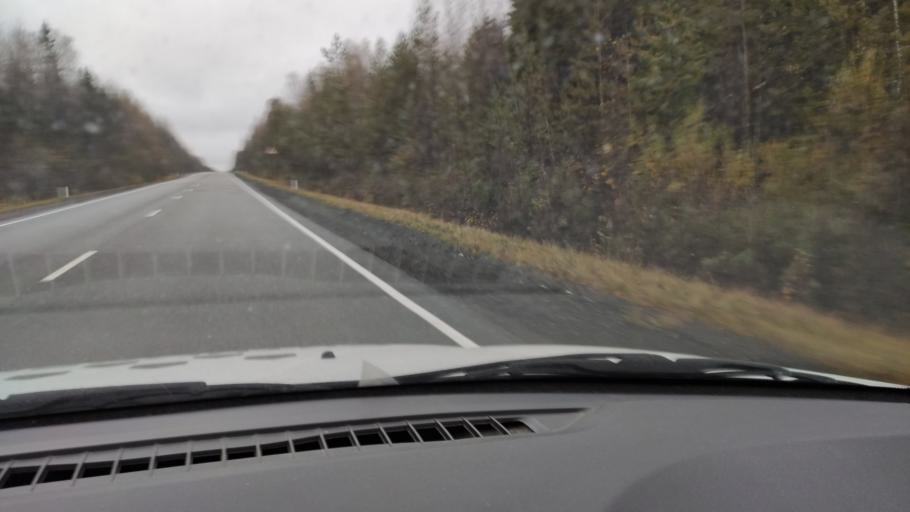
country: RU
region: Kirov
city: Chernaya Kholunitsa
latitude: 58.8686
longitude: 51.5577
